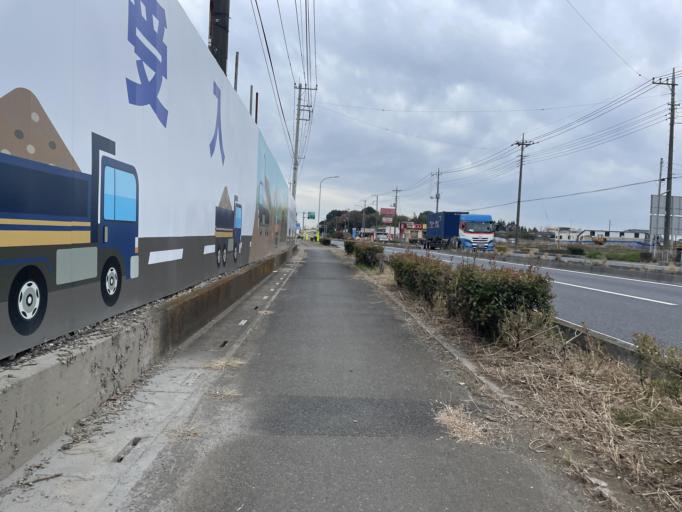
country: JP
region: Saitama
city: Shiraoka
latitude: 35.9983
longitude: 139.6492
